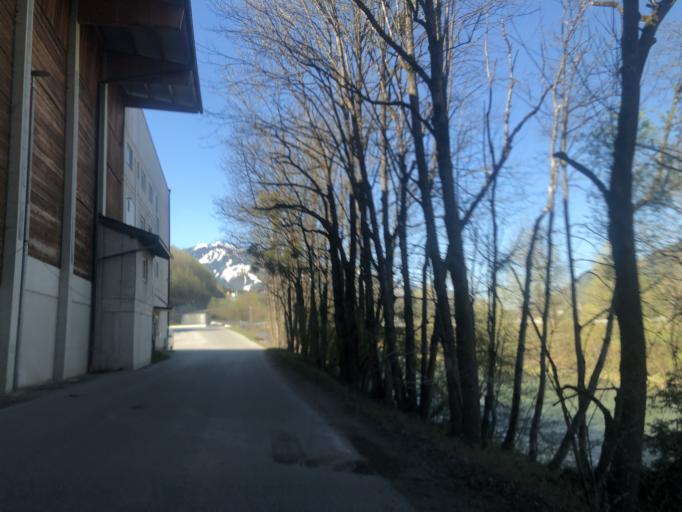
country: AT
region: Styria
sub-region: Politischer Bezirk Liezen
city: Schladming
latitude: 47.3994
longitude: 13.7079
